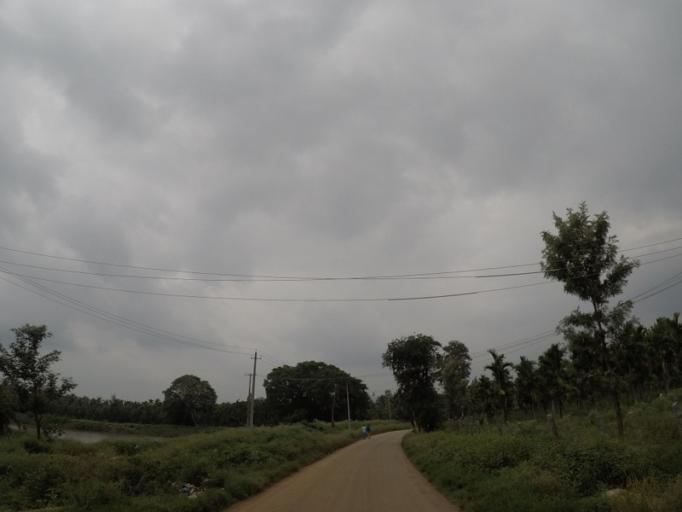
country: IN
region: Karnataka
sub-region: Chikmagalur
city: Tarikere
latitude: 13.5726
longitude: 75.8108
